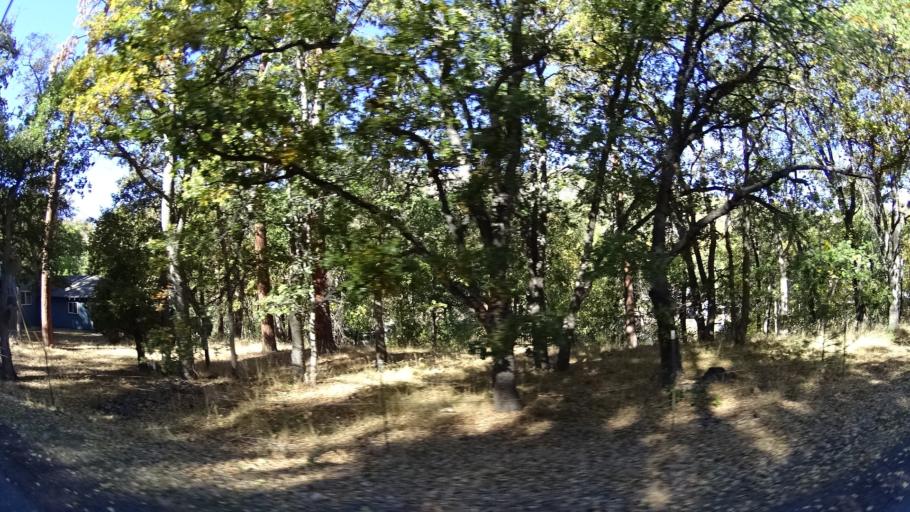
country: US
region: California
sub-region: Siskiyou County
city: Montague
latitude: 41.9705
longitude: -122.3025
